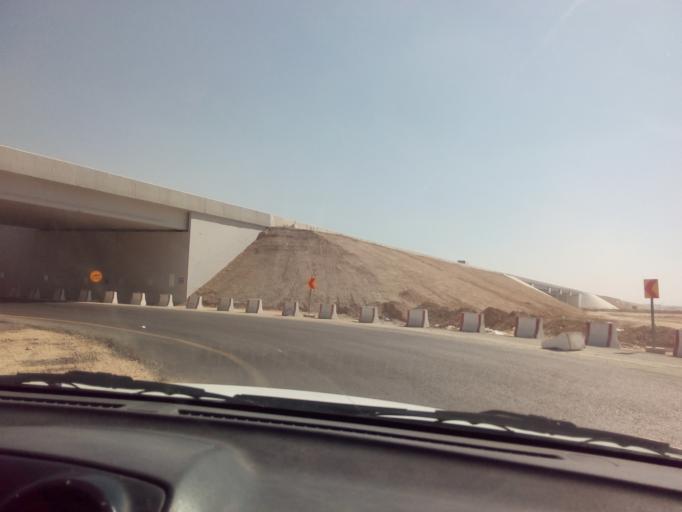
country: SA
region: Ar Riyad
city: Riyadh
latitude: 24.5952
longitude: 46.8860
